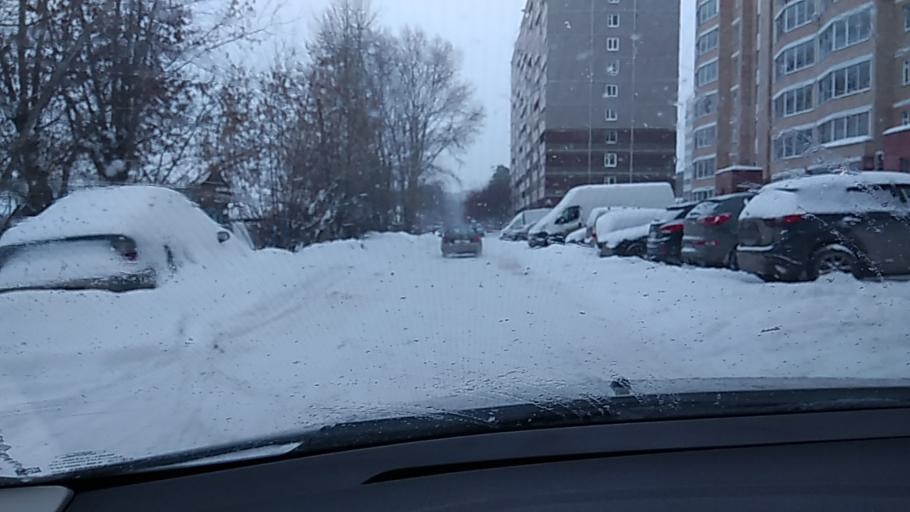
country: RU
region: Sverdlovsk
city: Sovkhoznyy
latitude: 56.8201
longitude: 60.5456
